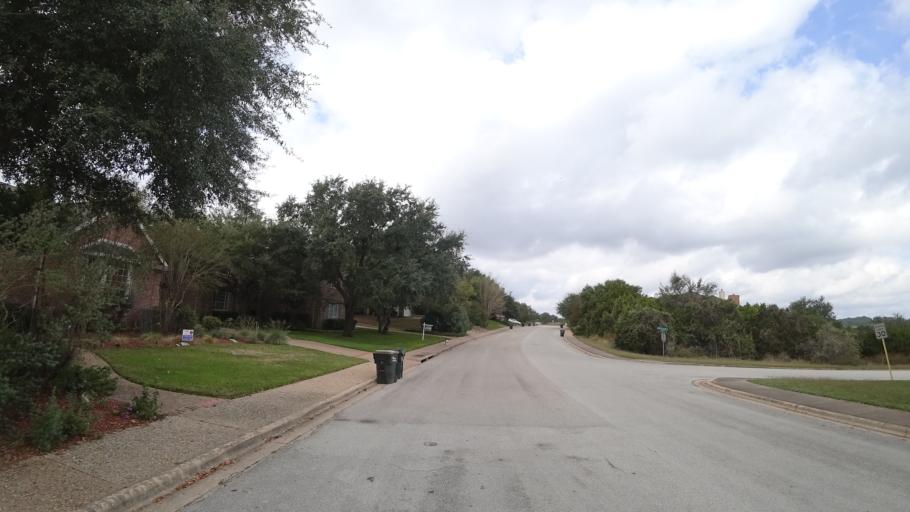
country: US
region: Texas
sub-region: Travis County
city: Barton Creek
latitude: 30.2959
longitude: -97.8873
